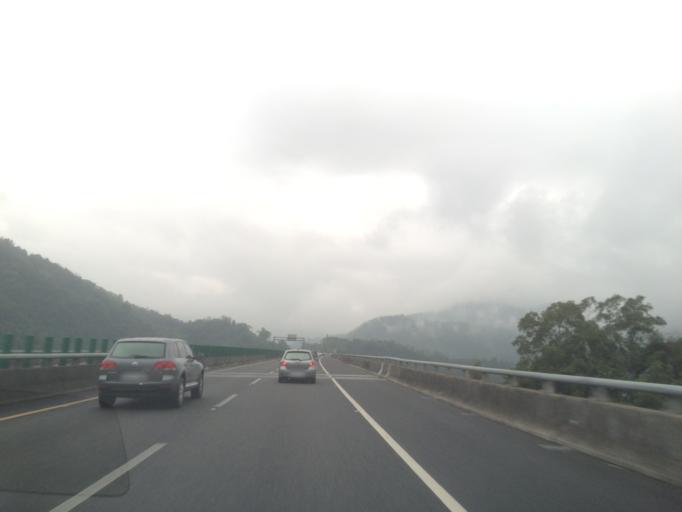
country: TW
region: Taiwan
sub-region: Nantou
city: Puli
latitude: 23.9797
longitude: 120.8975
